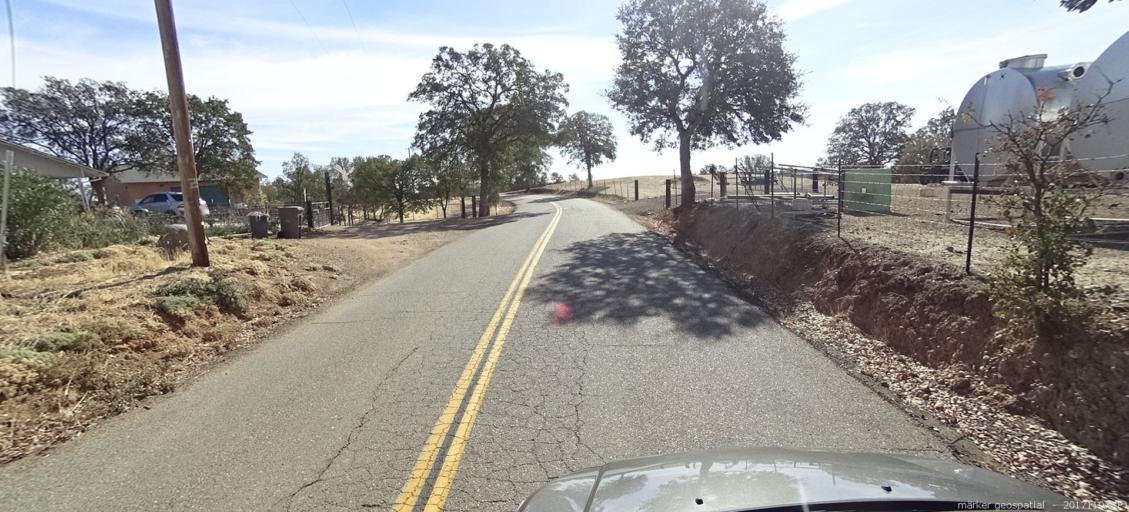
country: US
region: California
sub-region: Shasta County
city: Shasta
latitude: 40.4341
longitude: -122.5232
